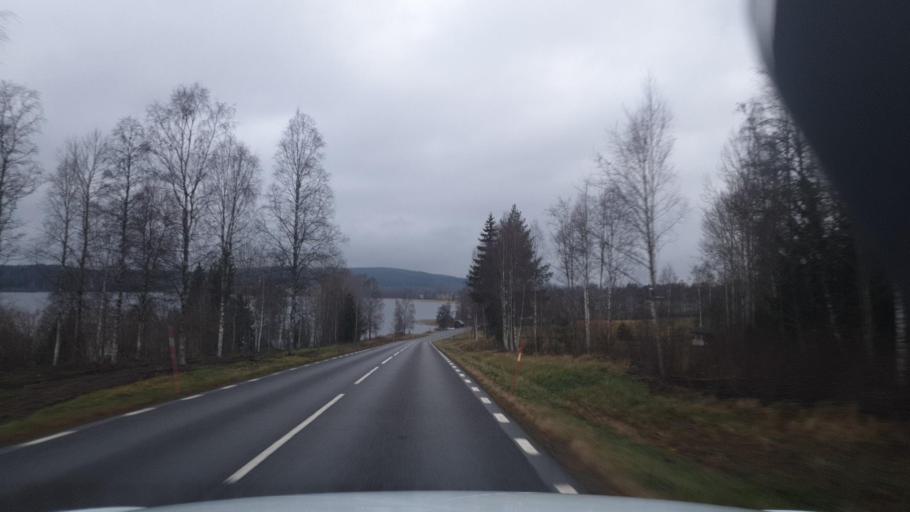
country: SE
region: Vaermland
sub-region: Arvika Kommun
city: Arvika
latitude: 59.7384
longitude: 12.5593
